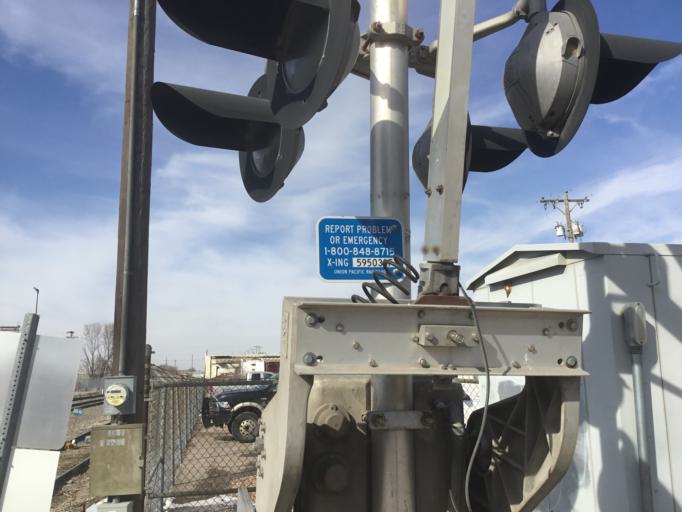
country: US
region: Kansas
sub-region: Sedgwick County
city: Wichita
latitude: 37.7117
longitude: -97.3285
